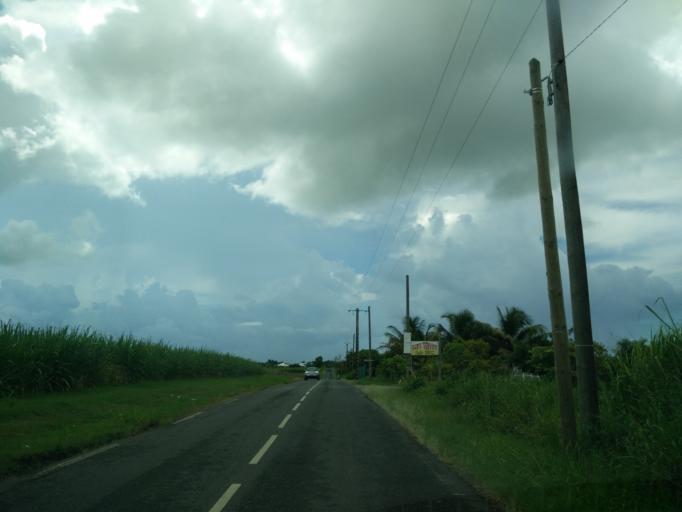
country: GP
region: Guadeloupe
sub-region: Guadeloupe
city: Le Moule
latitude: 16.2838
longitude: -61.3452
